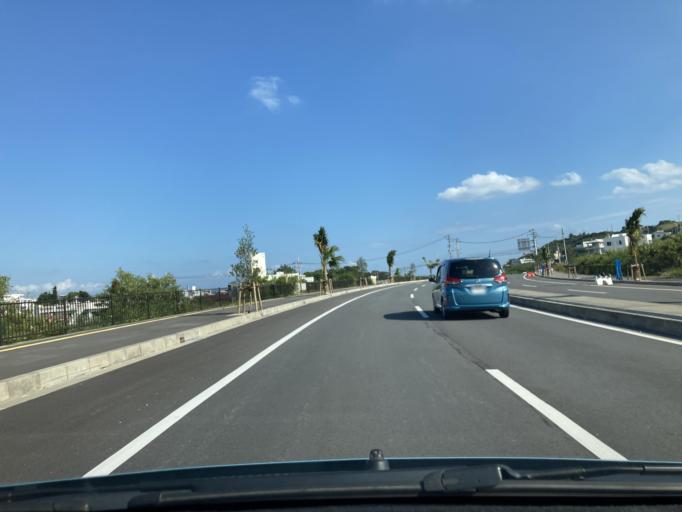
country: JP
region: Okinawa
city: Chatan
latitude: 26.3001
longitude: 127.7964
